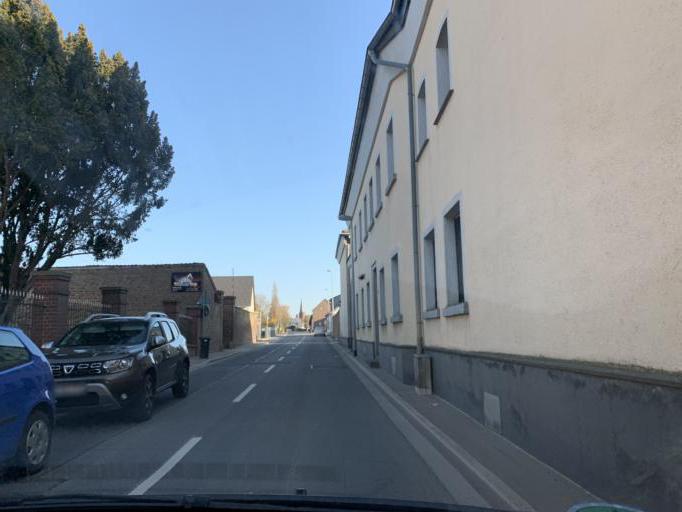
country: DE
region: North Rhine-Westphalia
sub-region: Regierungsbezirk Koln
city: Titz
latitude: 50.9996
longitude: 6.4878
